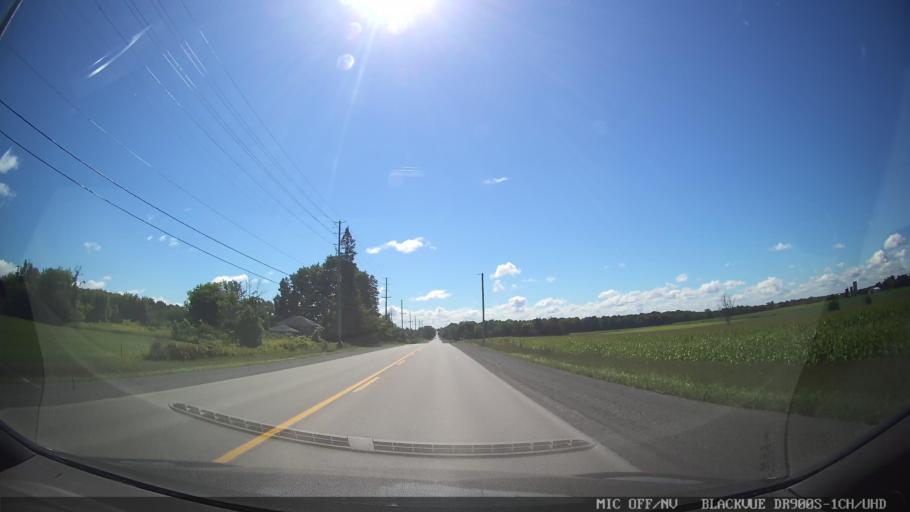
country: CA
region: Ontario
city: Bells Corners
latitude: 45.2645
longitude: -75.7999
